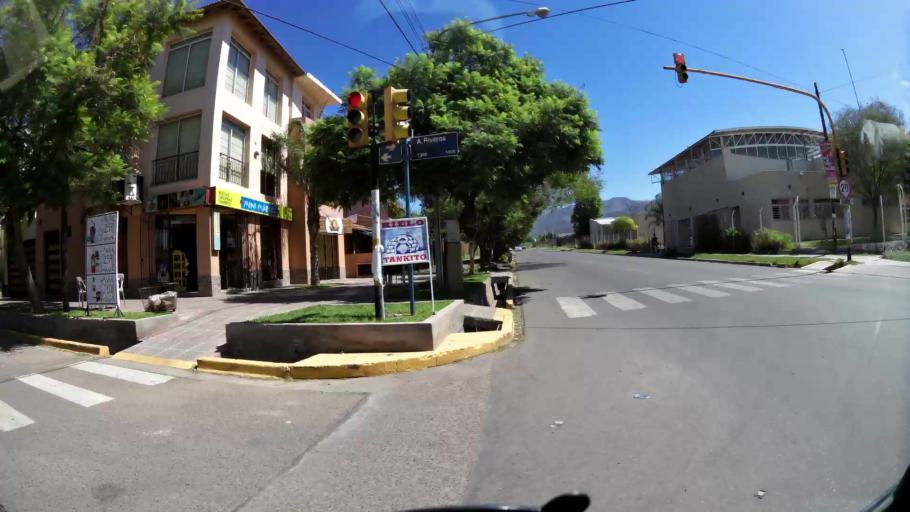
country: AR
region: Mendoza
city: Las Heras
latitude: -32.8517
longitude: -68.8534
